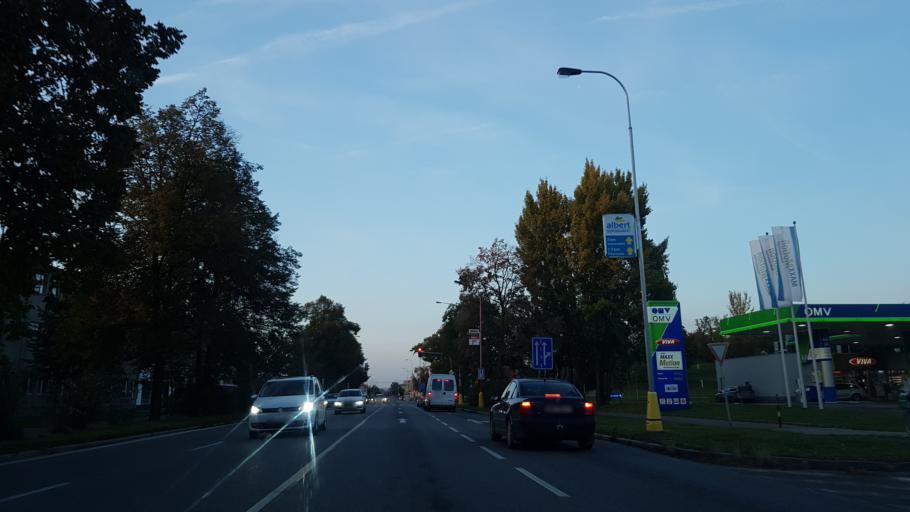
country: CZ
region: Zlin
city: Kunovice
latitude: 49.0559
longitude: 17.4666
